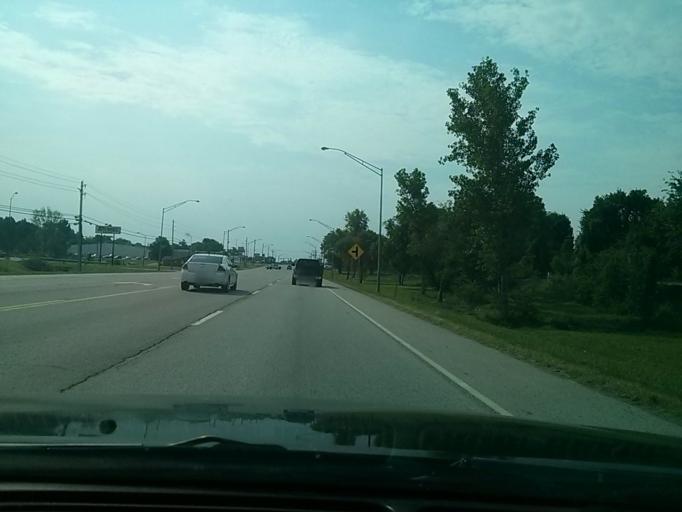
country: US
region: Oklahoma
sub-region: Wagoner County
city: Coweta
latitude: 35.9634
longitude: -95.6547
